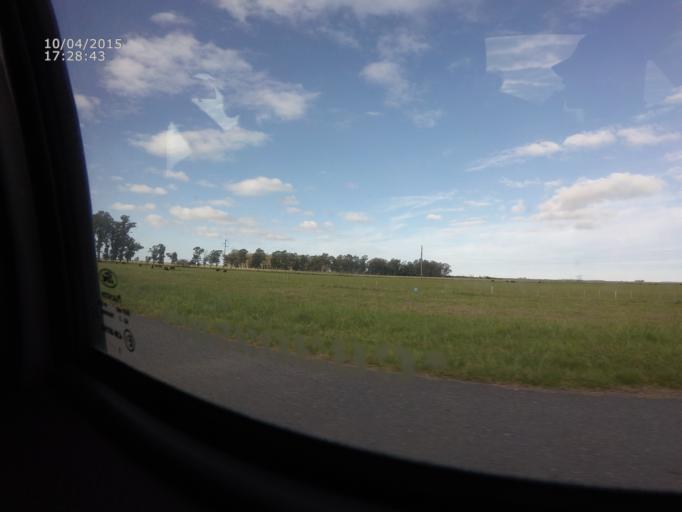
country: AR
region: Buenos Aires
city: Maipu
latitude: -37.0204
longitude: -57.8499
